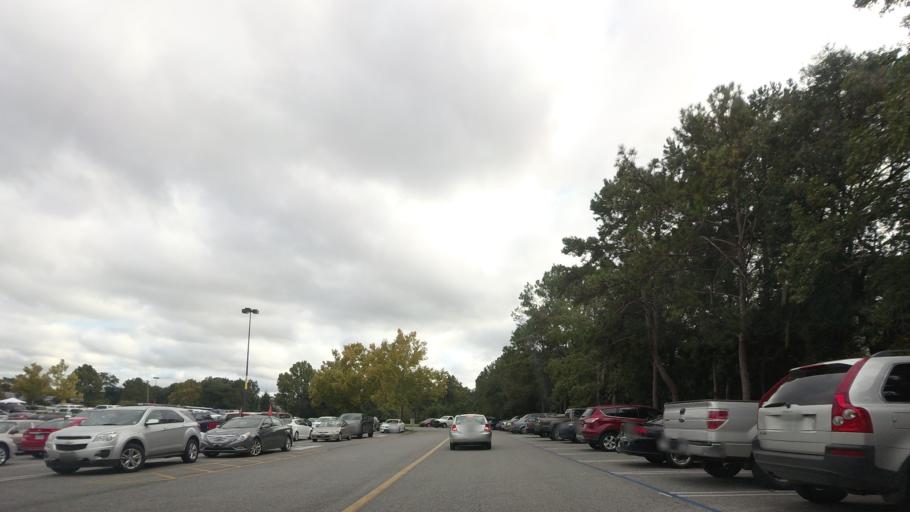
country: US
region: Florida
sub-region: Alachua County
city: Gainesville
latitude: 29.6540
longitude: -82.4118
